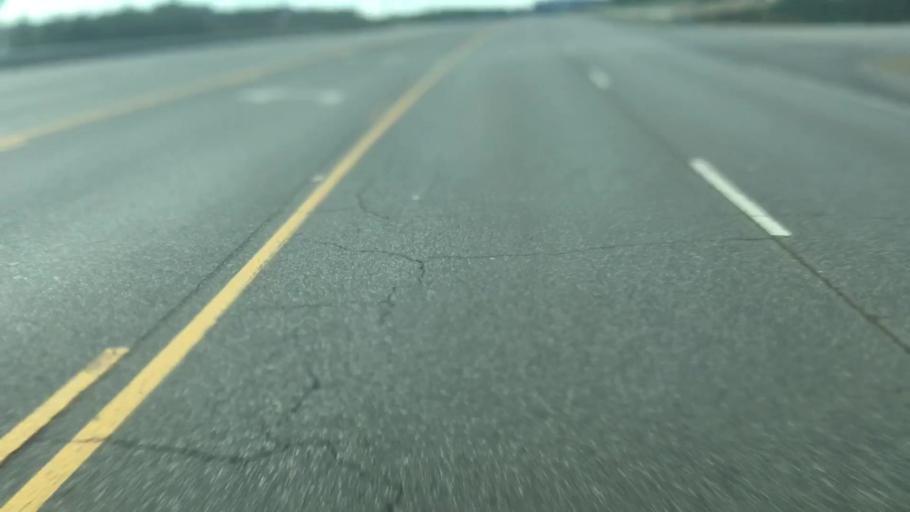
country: US
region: Alabama
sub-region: Walker County
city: Jasper
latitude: 33.8139
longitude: -87.2332
